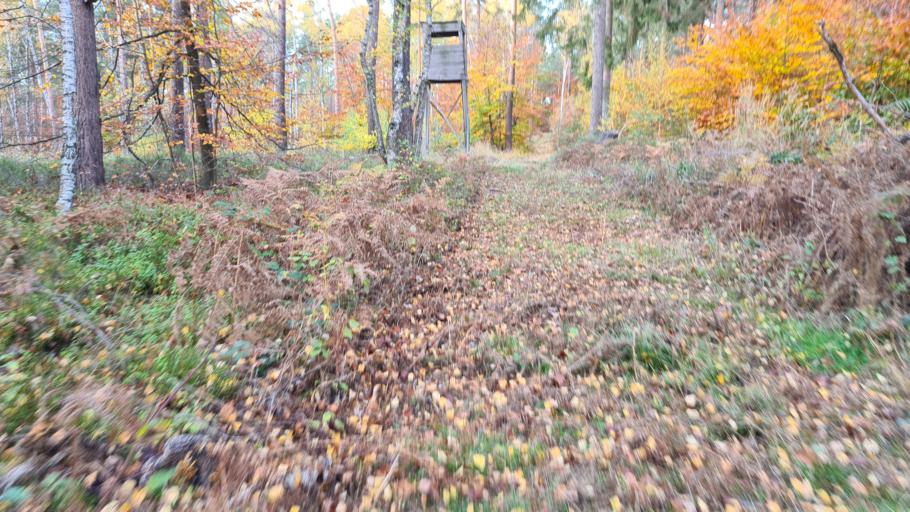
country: DE
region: Saxony
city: Dahlen
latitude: 51.4240
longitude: 13.0099
